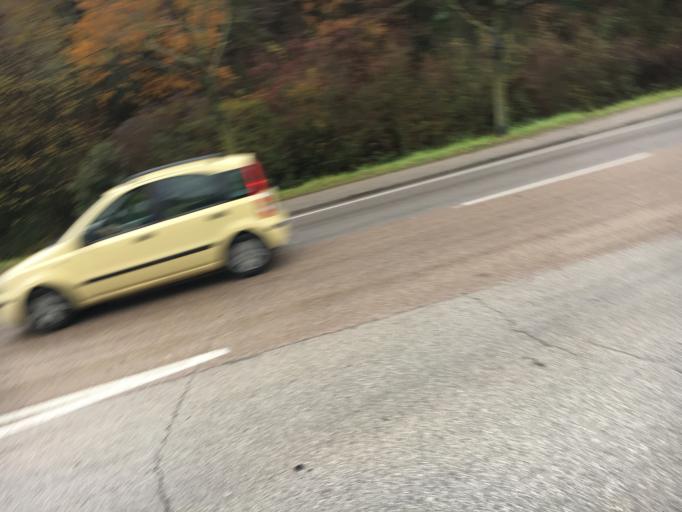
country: IT
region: Umbria
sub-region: Provincia di Perugia
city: Perugia
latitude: 43.1129
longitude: 12.3765
